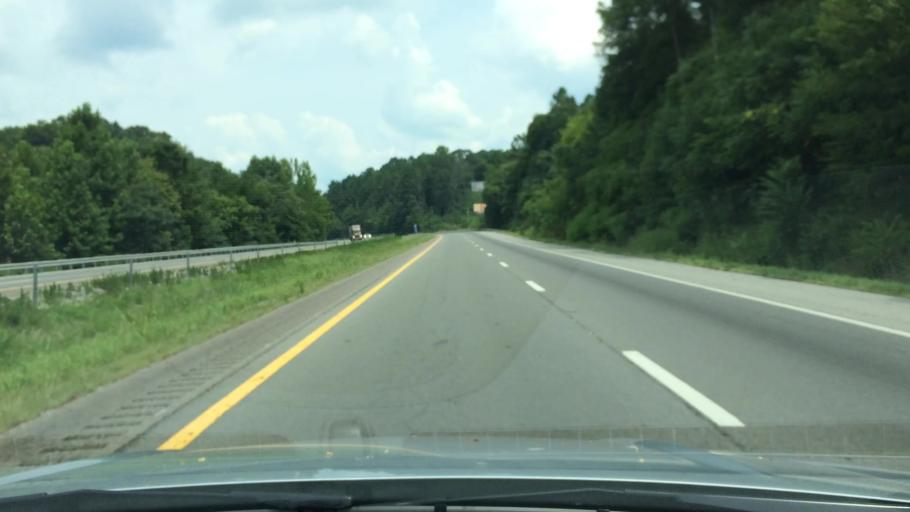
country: US
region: Tennessee
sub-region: Marshall County
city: Cornersville
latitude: 35.2574
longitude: -86.8829
